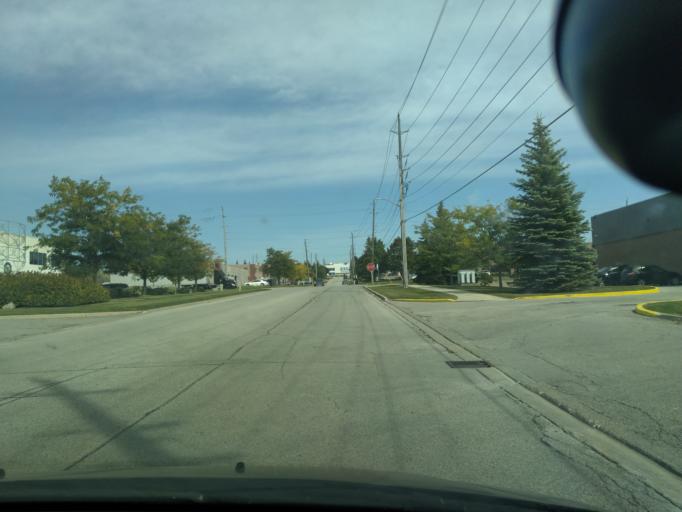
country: CA
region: Ontario
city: Newmarket
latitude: 44.0811
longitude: -79.4288
